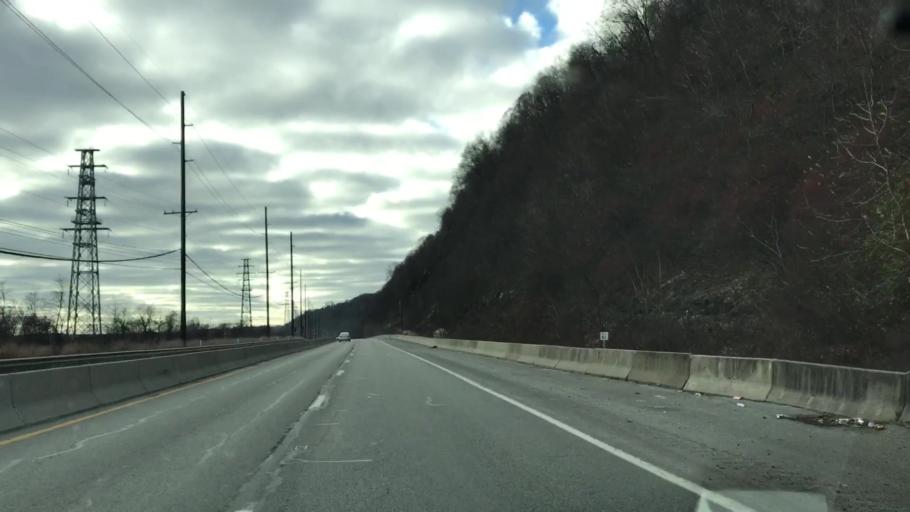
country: US
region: Pennsylvania
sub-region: Beaver County
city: Economy
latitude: 40.6135
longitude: -80.2424
